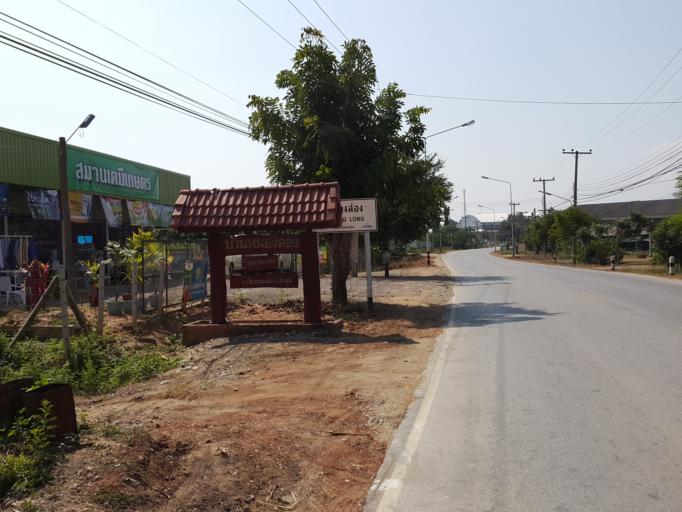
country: TH
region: Lamphun
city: Wiang Nong Long
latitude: 18.4113
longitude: 98.7473
